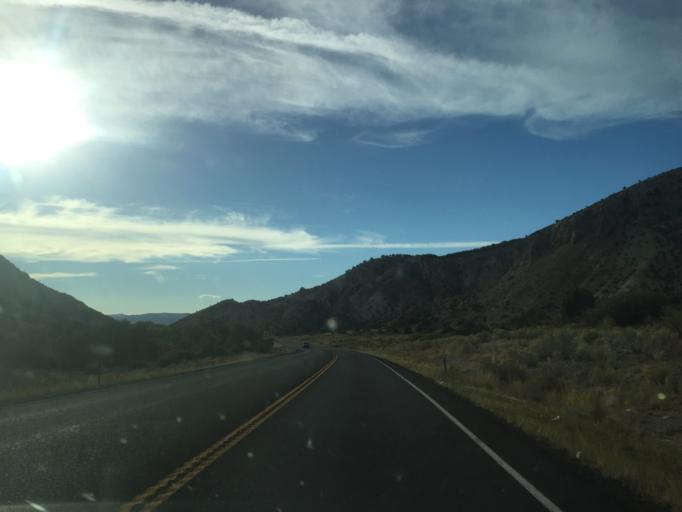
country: US
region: Utah
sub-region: Juab County
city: Nephi
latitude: 39.7139
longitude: -111.7840
